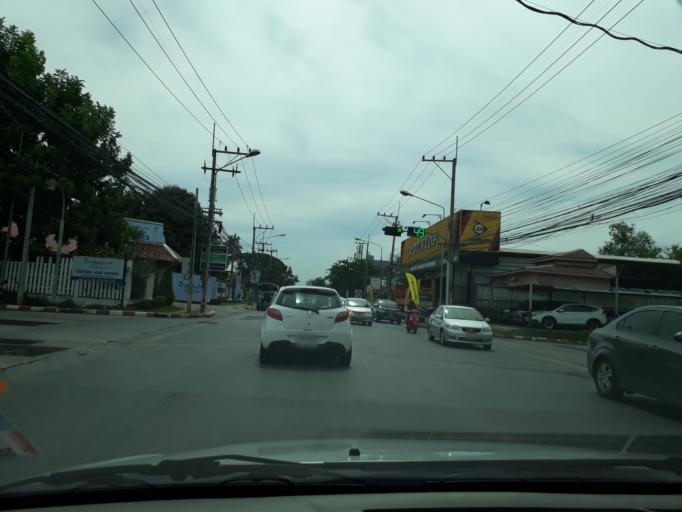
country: TH
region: Khon Kaen
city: Khon Kaen
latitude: 16.4372
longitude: 102.8442
